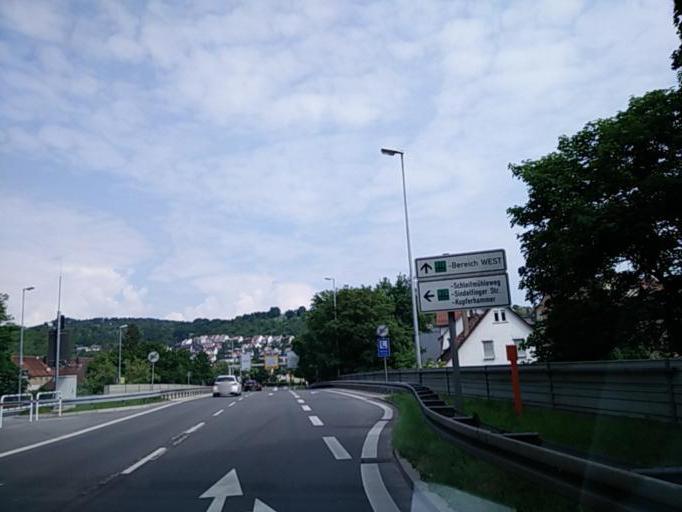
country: DE
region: Baden-Wuerttemberg
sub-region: Tuebingen Region
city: Tuebingen
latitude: 48.5175
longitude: 9.0448
